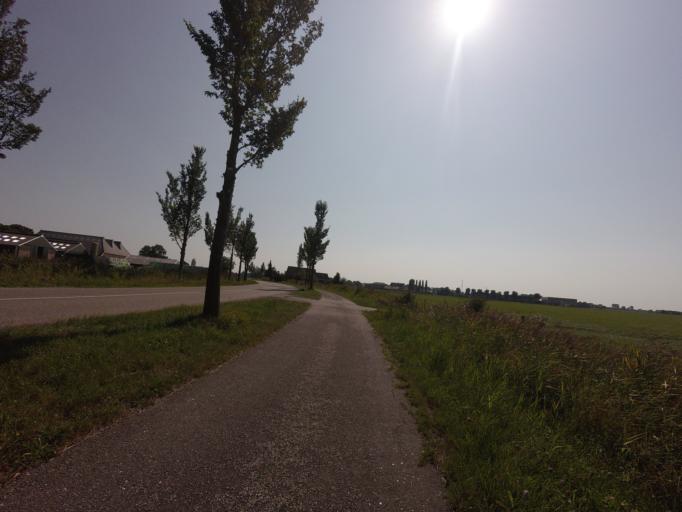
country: NL
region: Groningen
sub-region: Gemeente Zuidhorn
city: Grijpskerk
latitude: 53.2727
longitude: 6.3056
